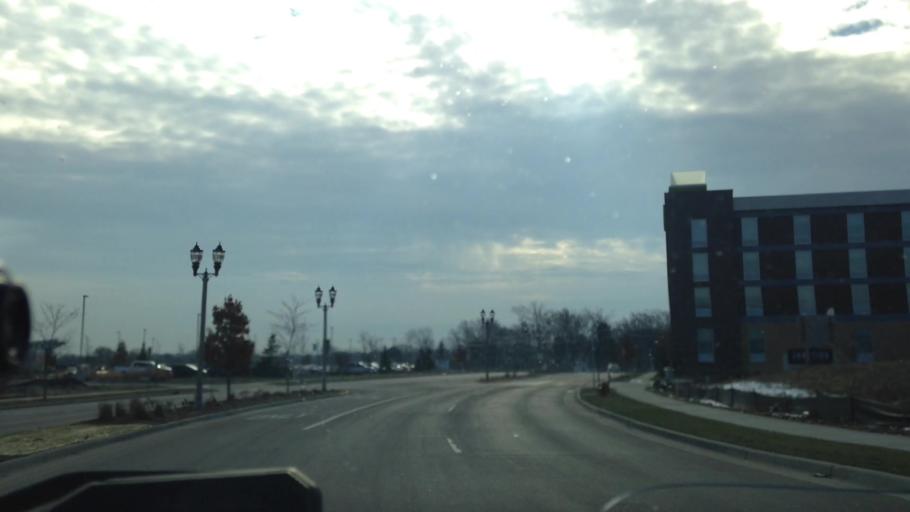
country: US
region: Wisconsin
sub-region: Waukesha County
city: Menomonee Falls
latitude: 43.1838
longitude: -88.1072
